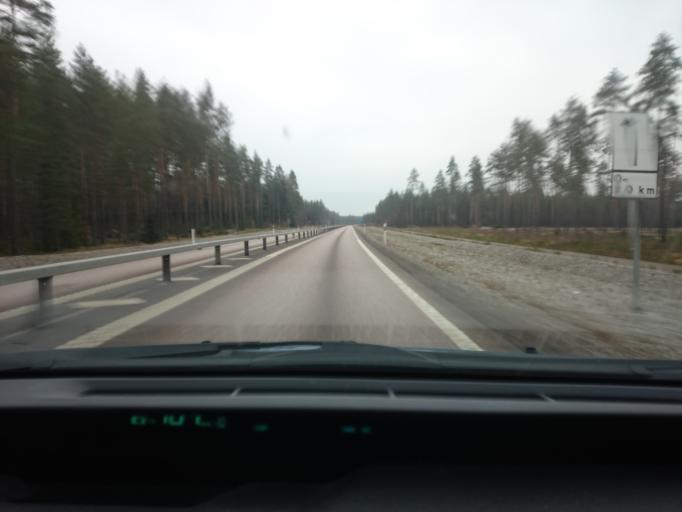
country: SE
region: Dalarna
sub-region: Avesta Kommun
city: Avesta
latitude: 60.0344
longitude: 16.3425
